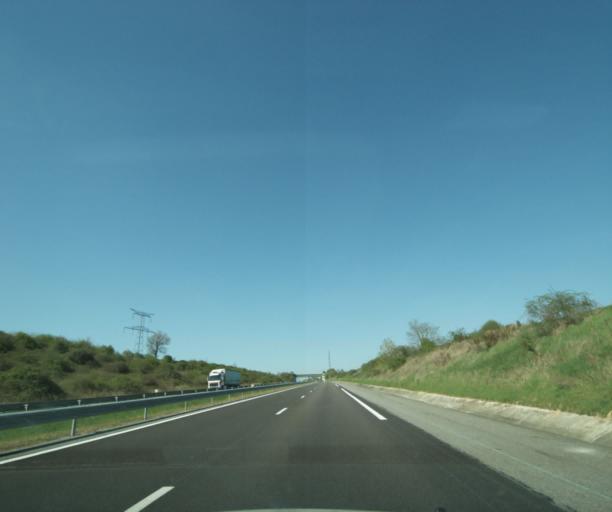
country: FR
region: Bourgogne
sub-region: Departement de la Nievre
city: Cosne-Cours-sur-Loire
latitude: 47.4550
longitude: 2.9480
